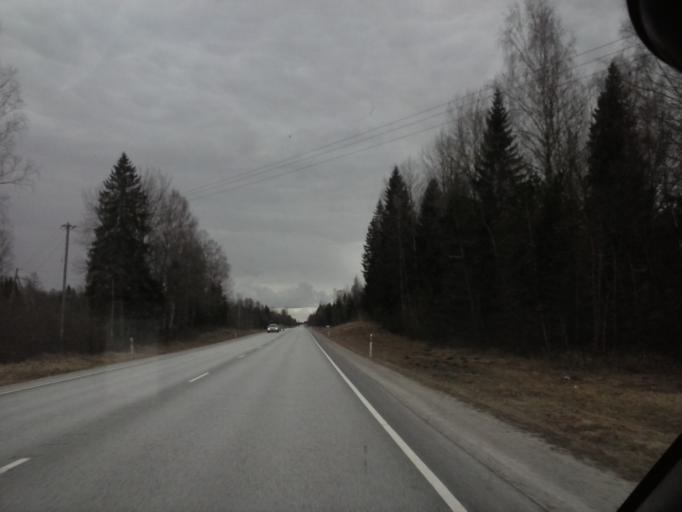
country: EE
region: Jaervamaa
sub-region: Paide linn
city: Paide
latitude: 58.9572
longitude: 25.6077
